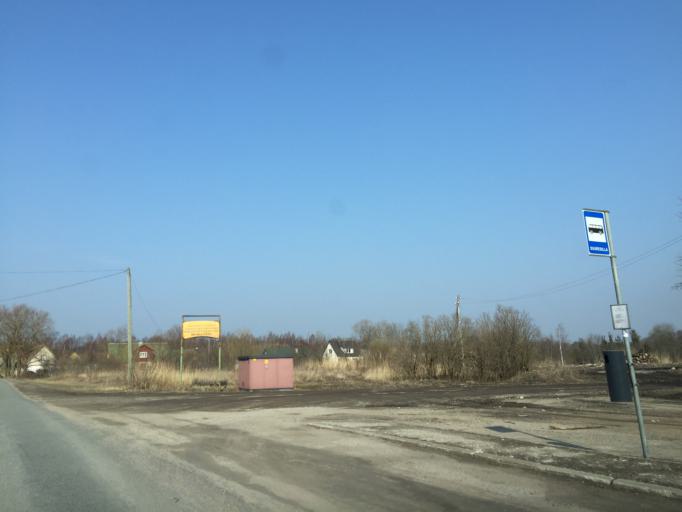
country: EE
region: Saare
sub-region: Kuressaare linn
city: Kuressaare
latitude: 58.2654
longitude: 22.4728
